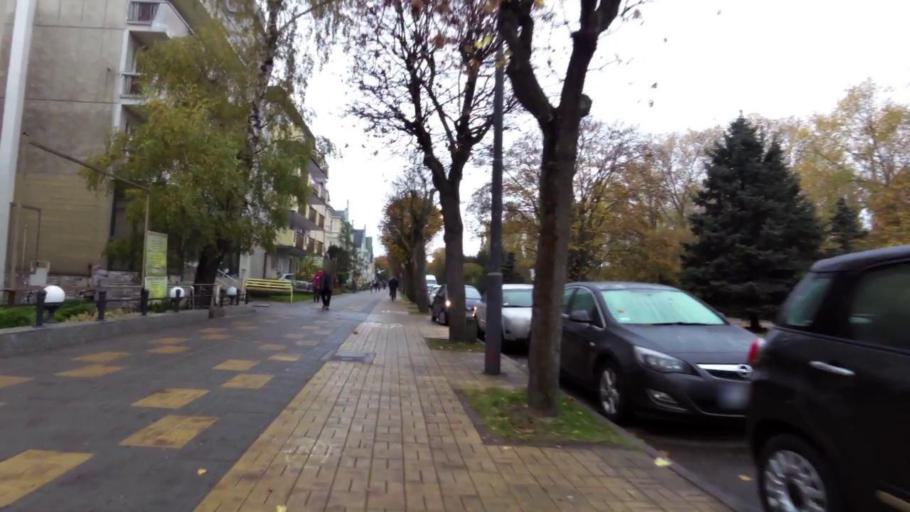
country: PL
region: West Pomeranian Voivodeship
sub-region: Swinoujscie
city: Swinoujscie
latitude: 53.9202
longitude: 14.2486
